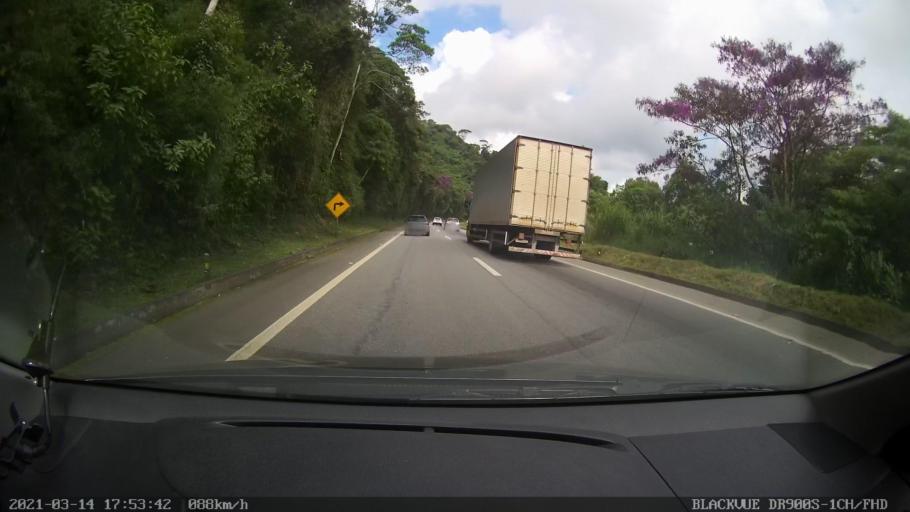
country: BR
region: Rio de Janeiro
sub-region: Petropolis
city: Petropolis
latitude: -22.4817
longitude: -43.2332
